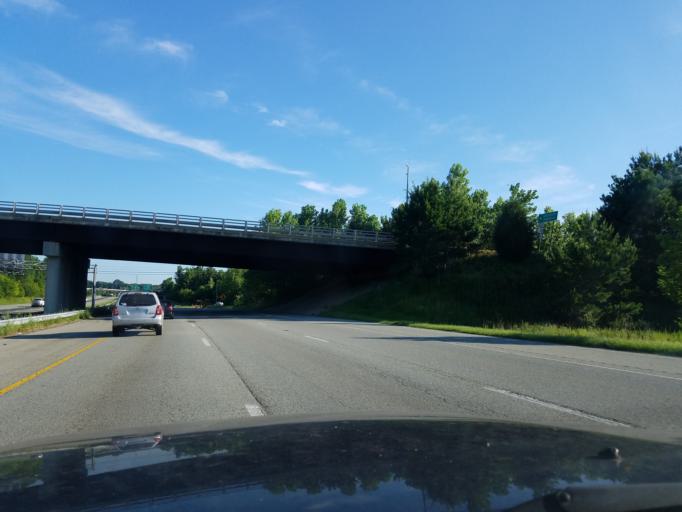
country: US
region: North Carolina
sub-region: Durham County
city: Durham
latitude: 36.0050
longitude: -78.8640
